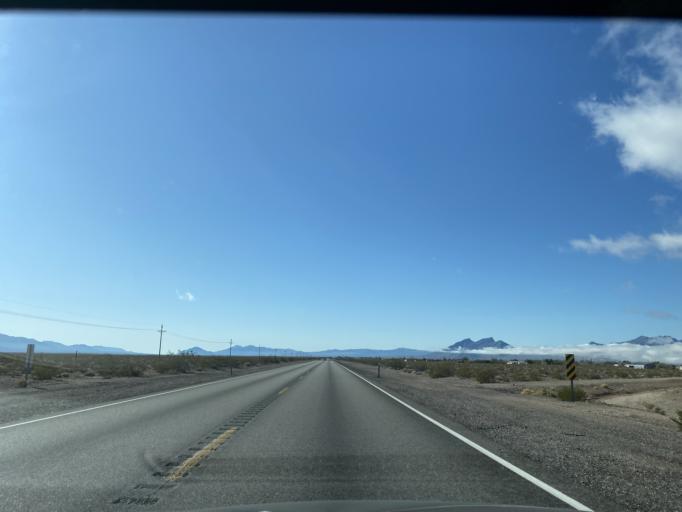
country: US
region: Nevada
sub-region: Nye County
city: Beatty
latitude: 36.5215
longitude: -116.4196
